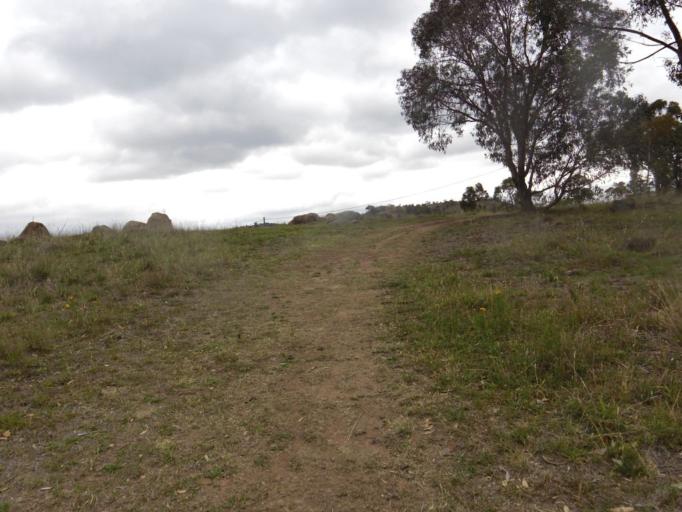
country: AU
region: Australian Capital Territory
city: Macarthur
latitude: -35.3627
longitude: 149.0378
